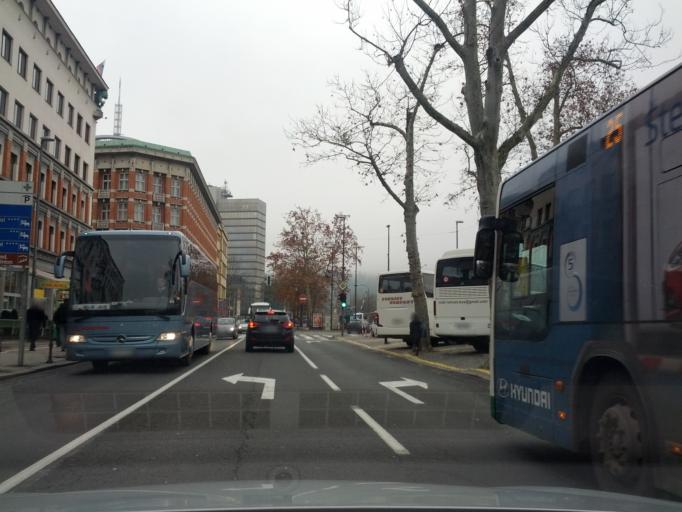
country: SI
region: Ljubljana
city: Ljubljana
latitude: 46.0576
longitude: 14.5095
